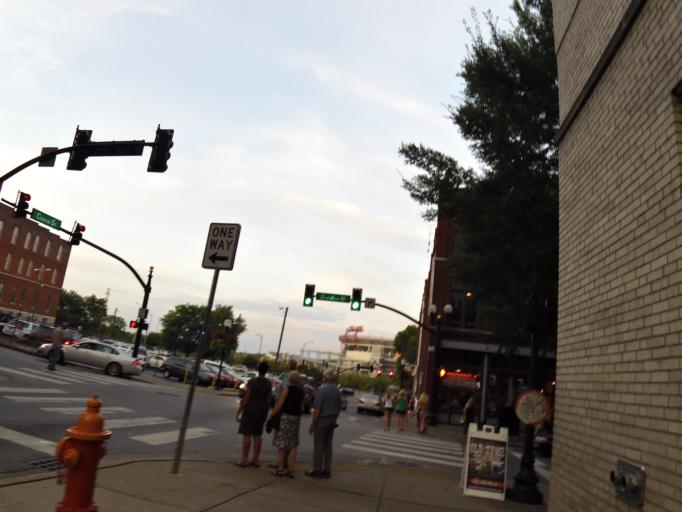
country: US
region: Tennessee
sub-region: Davidson County
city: Nashville
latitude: 36.1645
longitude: -86.7771
